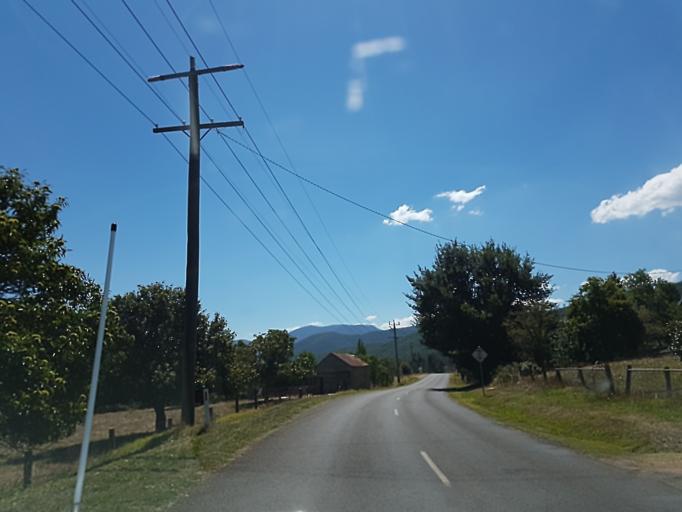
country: AU
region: Victoria
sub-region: Alpine
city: Mount Beauty
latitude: -36.7592
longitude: 146.9833
